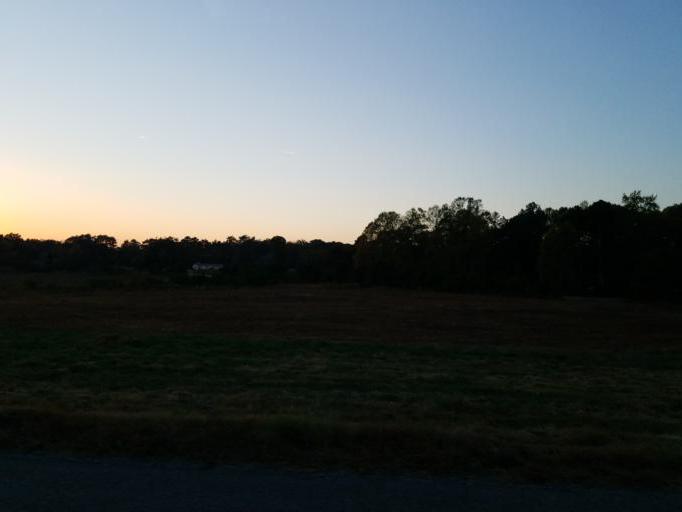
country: US
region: Georgia
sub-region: Dawson County
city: Dawsonville
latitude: 34.3273
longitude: -84.0578
